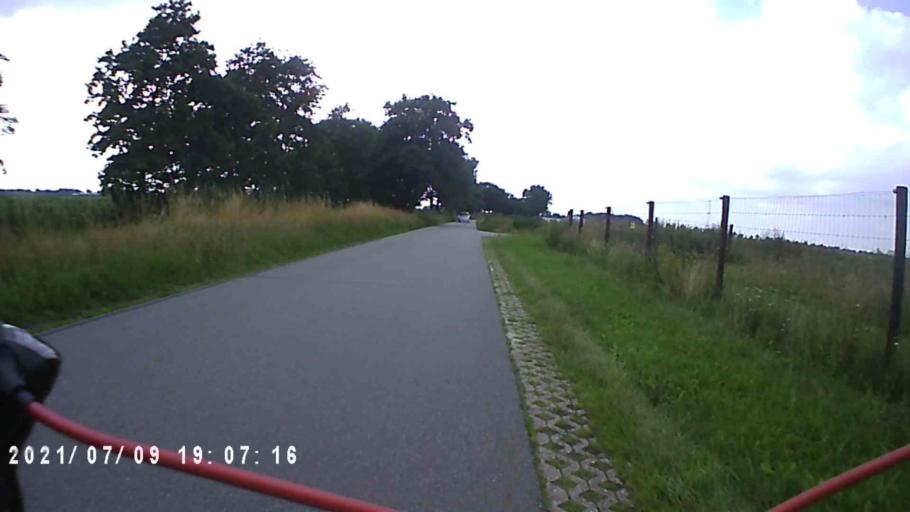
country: NL
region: Groningen
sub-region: Gemeente Veendam
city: Veendam
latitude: 53.0596
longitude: 6.8762
